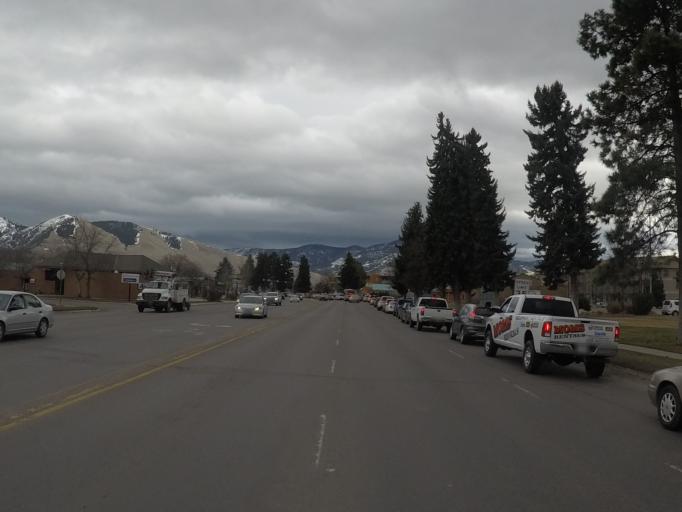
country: US
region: Montana
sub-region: Missoula County
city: Missoula
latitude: 46.8801
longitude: -114.0214
